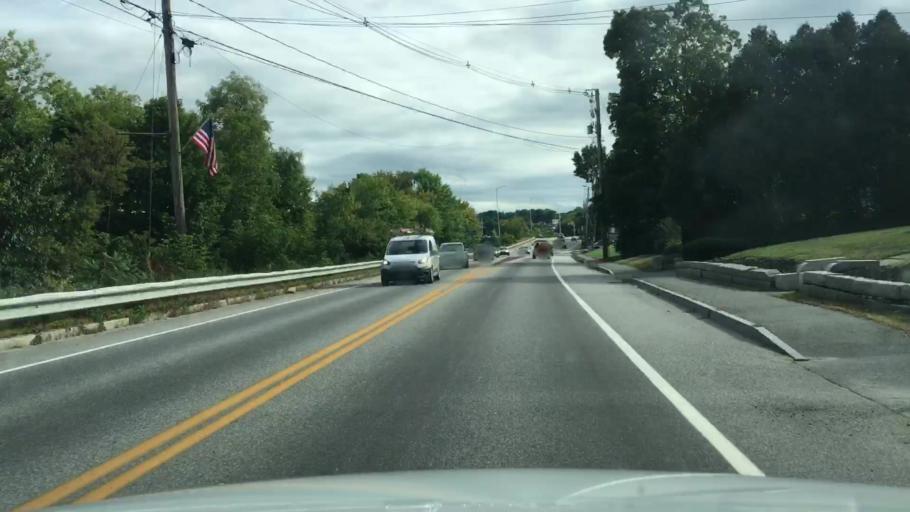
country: US
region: Maine
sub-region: Kennebec County
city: Farmingdale
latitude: 44.2369
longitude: -69.7718
